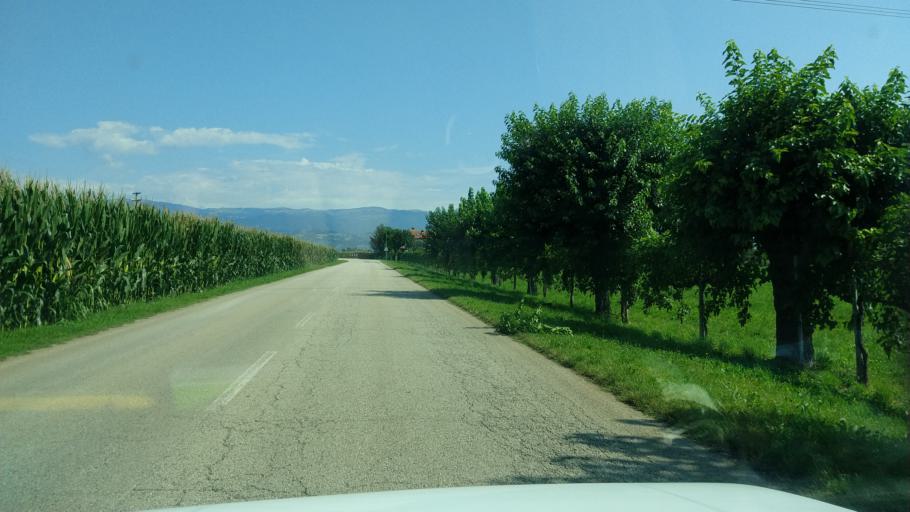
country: IT
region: Veneto
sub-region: Provincia di Vicenza
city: Sandrigo
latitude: 45.6784
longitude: 11.6096
